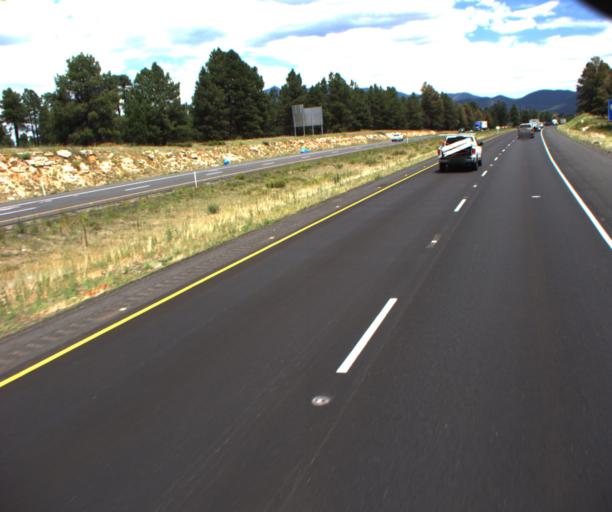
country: US
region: Arizona
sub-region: Coconino County
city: Flagstaff
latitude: 35.1551
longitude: -111.6794
